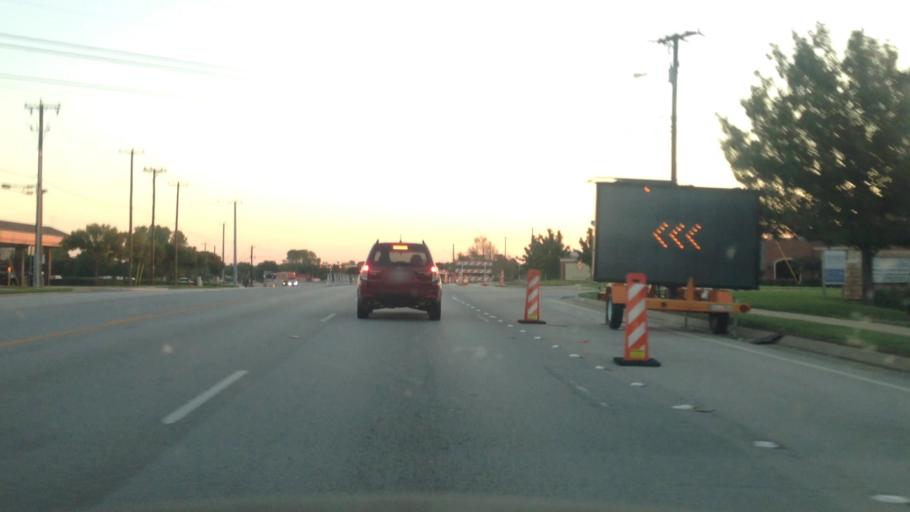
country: US
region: Texas
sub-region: Tarrant County
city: North Richland Hills
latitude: 32.8601
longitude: -97.2104
